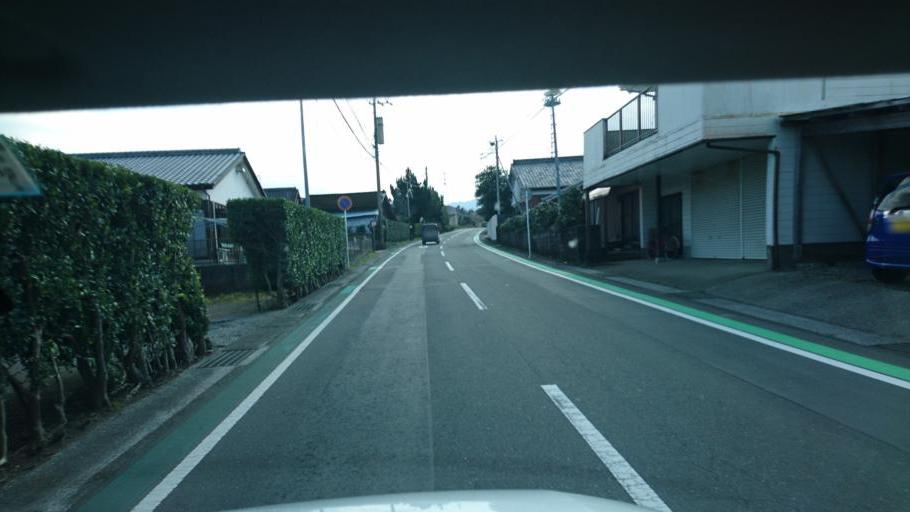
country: JP
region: Miyazaki
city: Miyazaki-shi
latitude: 31.8398
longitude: 131.3936
